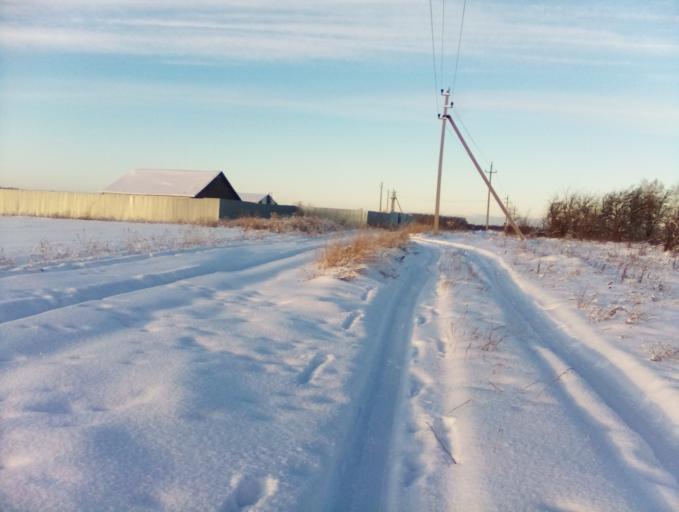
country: RU
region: Chelyabinsk
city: Poletayevo
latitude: 54.9838
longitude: 60.9471
